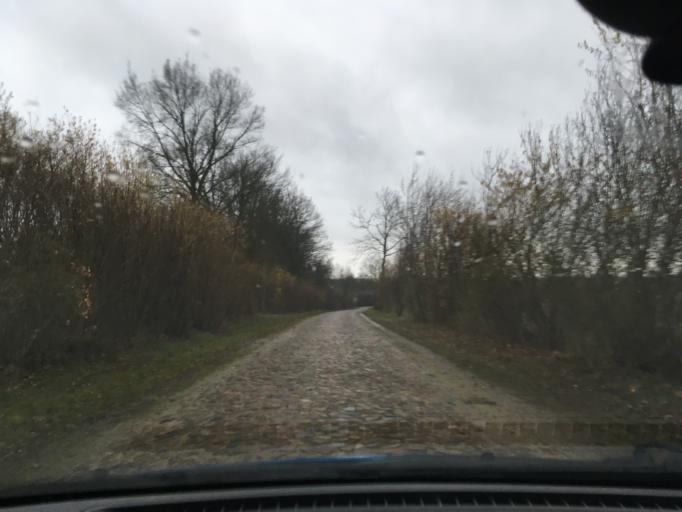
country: DE
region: Schleswig-Holstein
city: Kruzen
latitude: 53.4094
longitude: 10.5229
